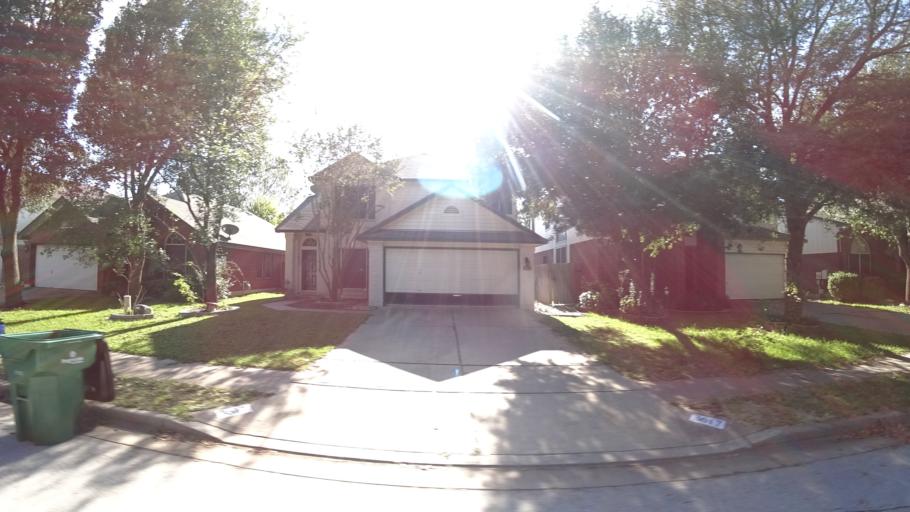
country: US
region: Texas
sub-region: Travis County
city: Wells Branch
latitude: 30.4615
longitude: -97.6832
